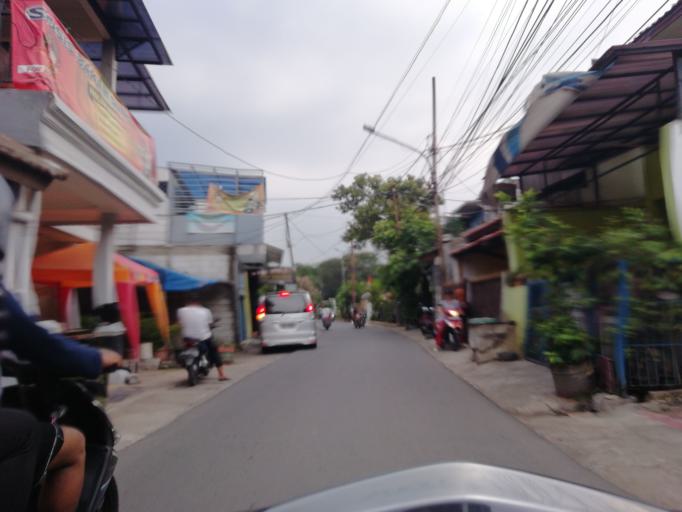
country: ID
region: West Java
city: Depok
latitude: -6.3310
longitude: 106.8208
